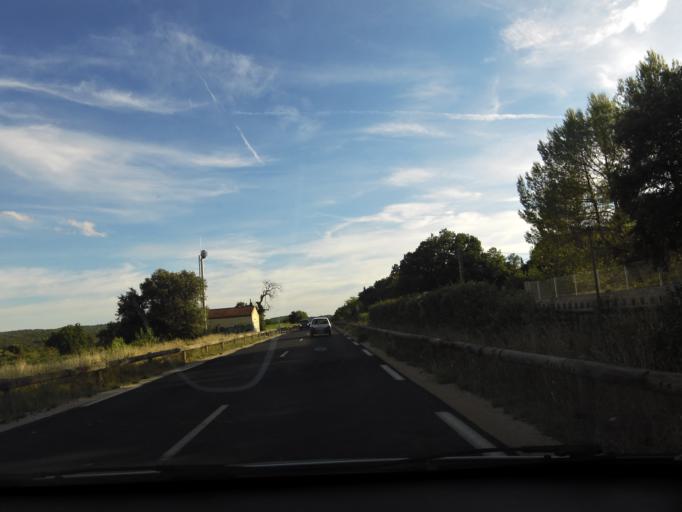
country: FR
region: Languedoc-Roussillon
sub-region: Departement de l'Herault
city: Claret
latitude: 43.8392
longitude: 3.9153
